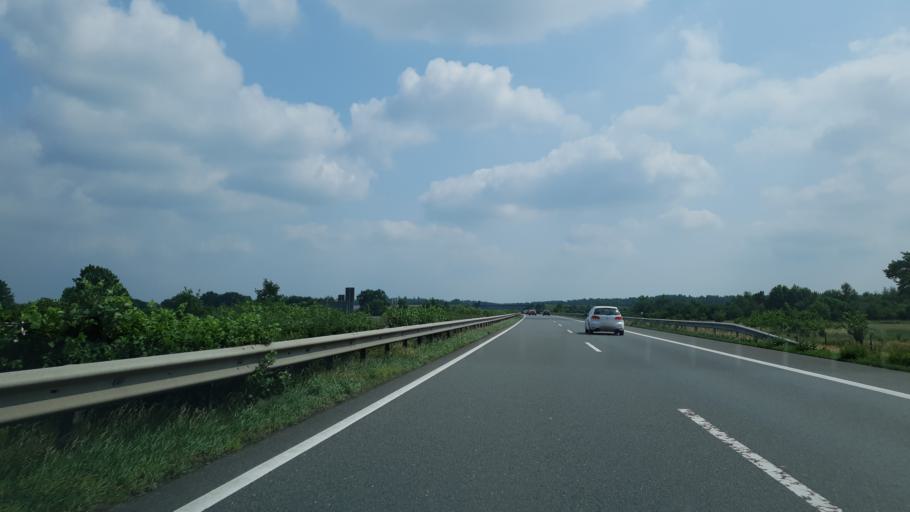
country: DE
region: Lower Saxony
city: Engden
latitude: 52.4799
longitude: 7.2128
